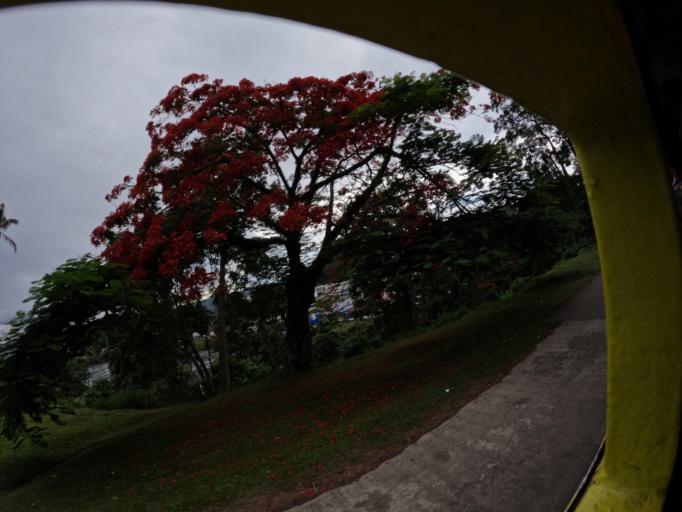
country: FJ
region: Central
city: Suva
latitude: -18.1303
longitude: 178.4348
